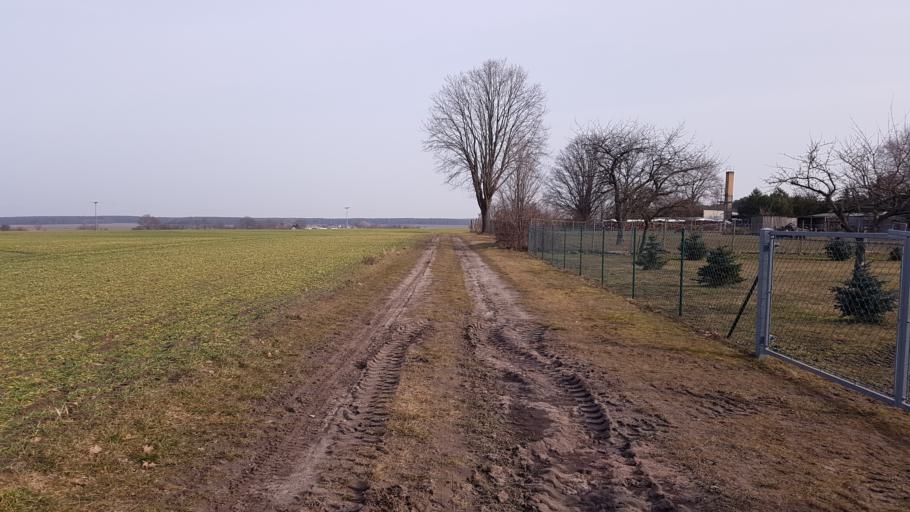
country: DE
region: Brandenburg
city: Sonnewalde
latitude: 51.6924
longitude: 13.6826
